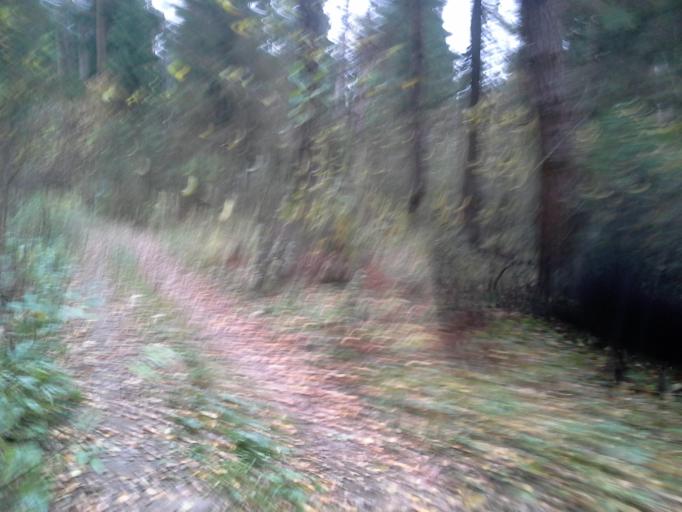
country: RU
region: Moskovskaya
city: Gorki Vtoryye
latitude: 55.6854
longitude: 37.1623
